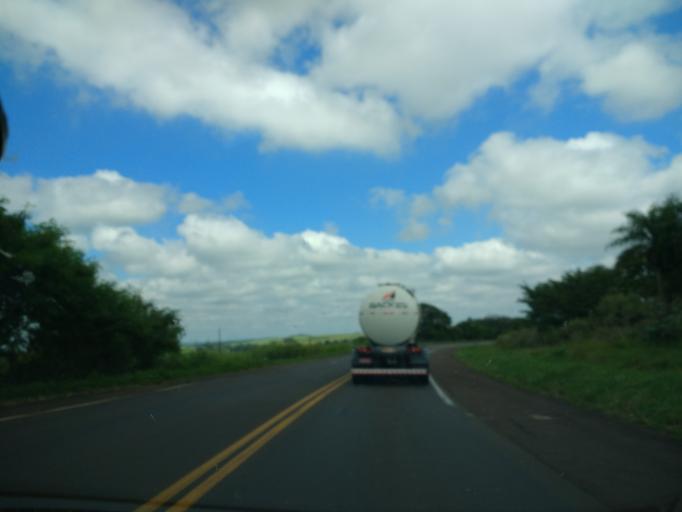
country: BR
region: Parana
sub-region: Cruzeiro Do Oeste
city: Cruzeiro do Oeste
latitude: -23.7863
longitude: -53.0266
